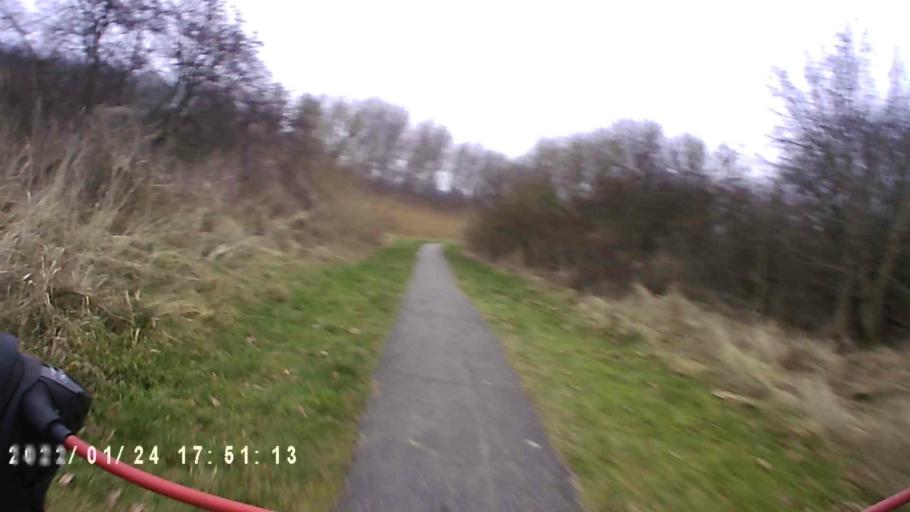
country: NL
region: Friesland
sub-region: Gemeente Schiermonnikoog
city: Schiermonnikoog
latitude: 53.4089
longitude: 6.2269
